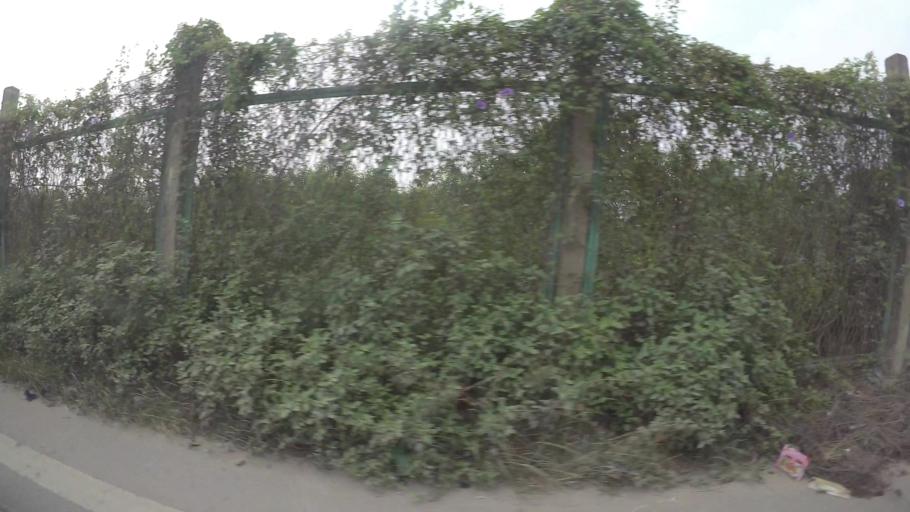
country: VN
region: Ha Noi
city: Quoc Oai
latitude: 21.0048
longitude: 105.6790
